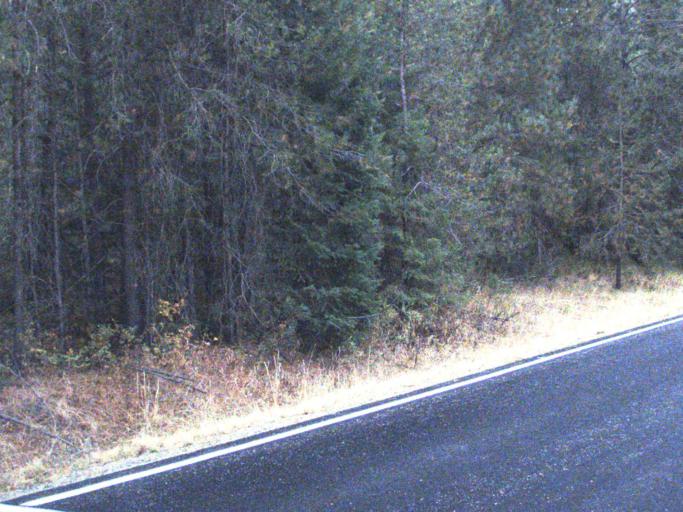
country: US
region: Washington
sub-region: Stevens County
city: Chewelah
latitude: 48.1345
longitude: -117.7386
